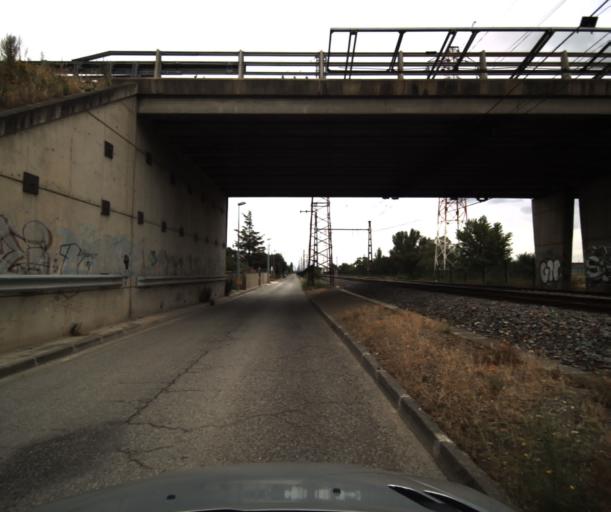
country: FR
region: Midi-Pyrenees
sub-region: Departement de la Haute-Garonne
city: Portet-sur-Garonne
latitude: 43.5348
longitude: 1.3947
